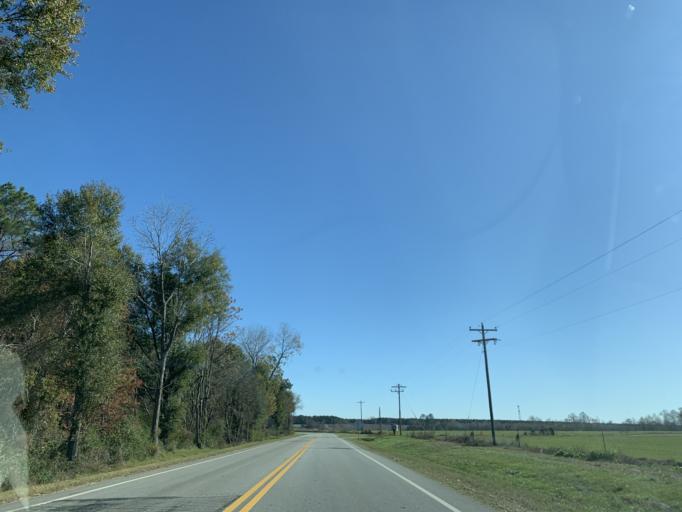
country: US
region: Georgia
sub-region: Ben Hill County
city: Fitzgerald
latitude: 31.7132
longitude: -83.1902
